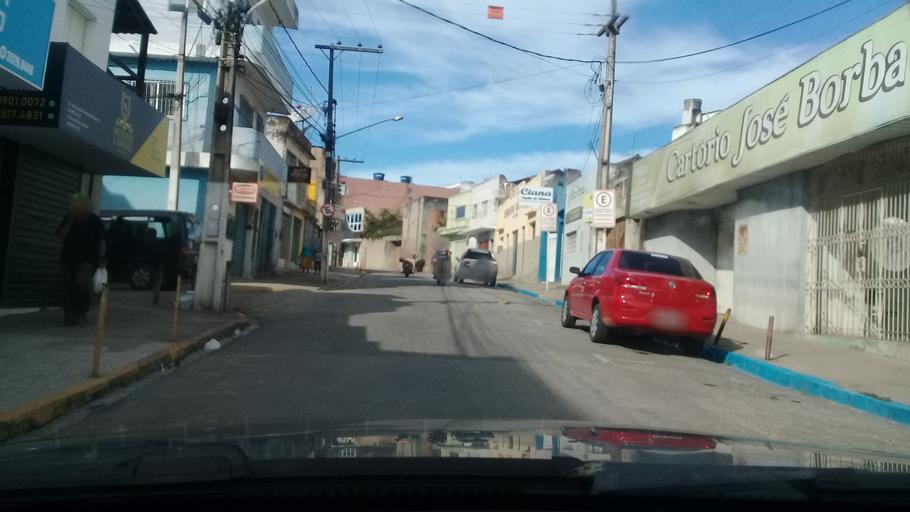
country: BR
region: Pernambuco
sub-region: Vitoria De Santo Antao
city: Vitoria de Santo Antao
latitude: -8.1173
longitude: -35.2959
